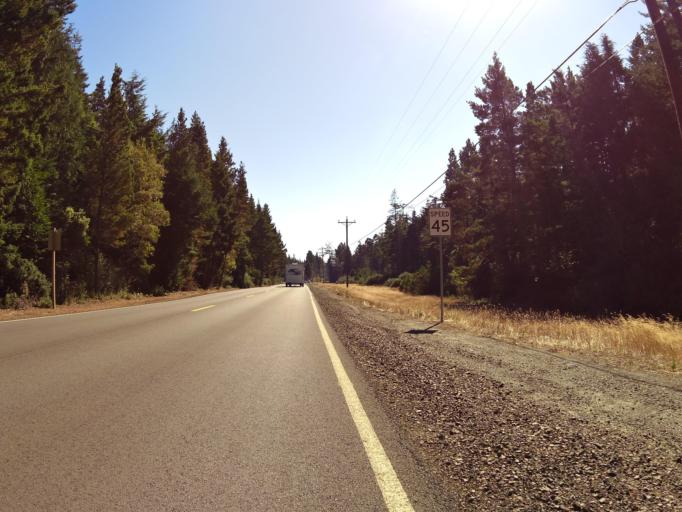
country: US
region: Oregon
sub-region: Coos County
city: Bandon
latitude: 43.1896
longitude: -124.3676
